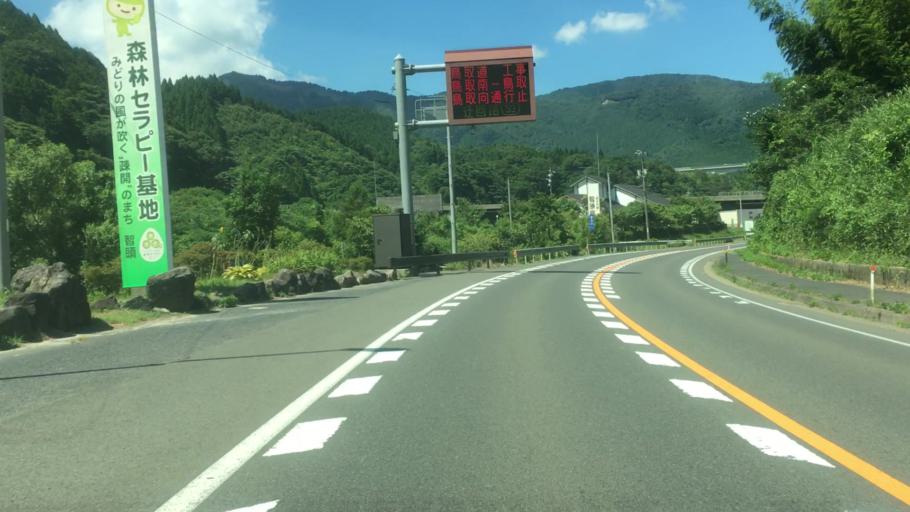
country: JP
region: Tottori
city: Tottori
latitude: 35.2753
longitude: 134.2241
